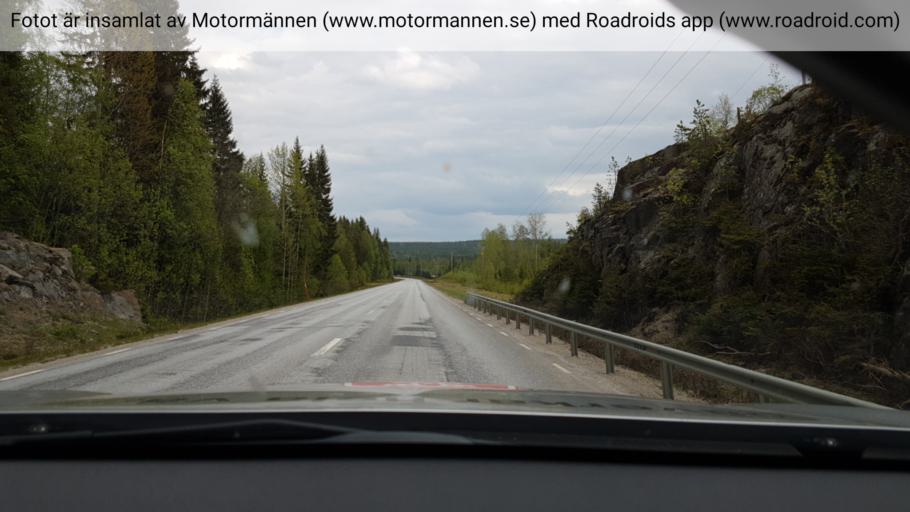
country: SE
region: Vaesterbotten
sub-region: Bjurholms Kommun
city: Bjurholm
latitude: 63.9297
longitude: 19.2773
